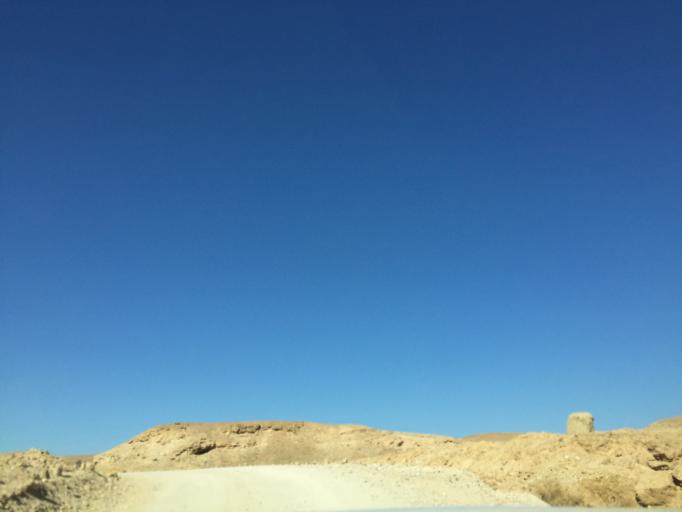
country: IL
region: Southern District
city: Mitzpe Ramon
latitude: 30.6130
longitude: 34.9333
